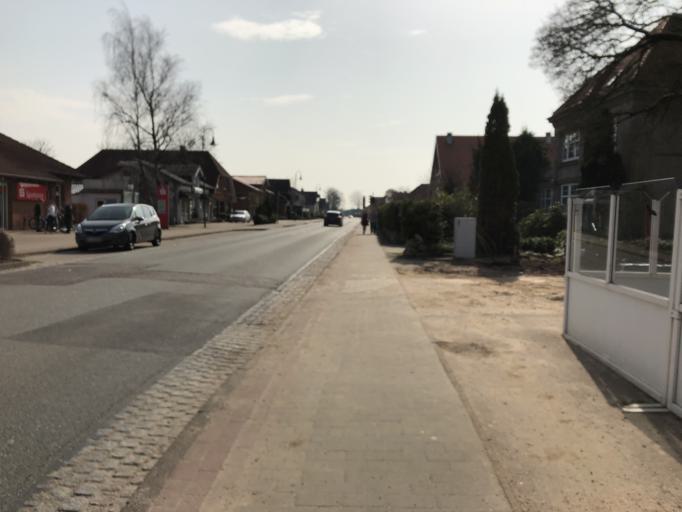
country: DE
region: Schleswig-Holstein
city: Tarp
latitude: 54.6626
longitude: 9.3991
